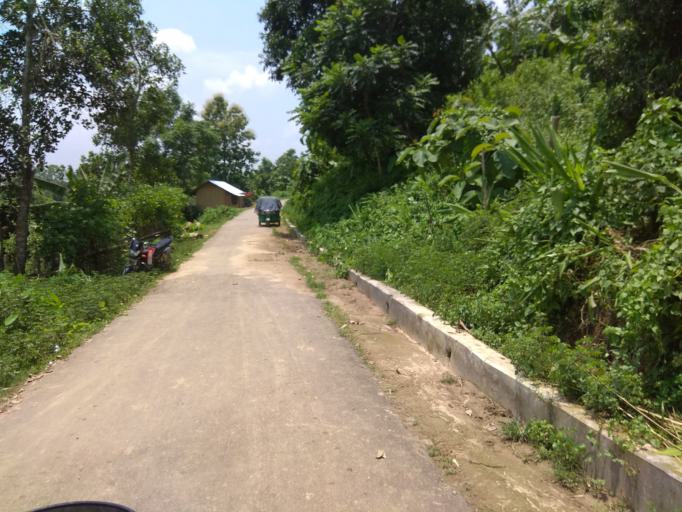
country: BD
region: Chittagong
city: Manikchari
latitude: 22.8968
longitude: 91.9240
